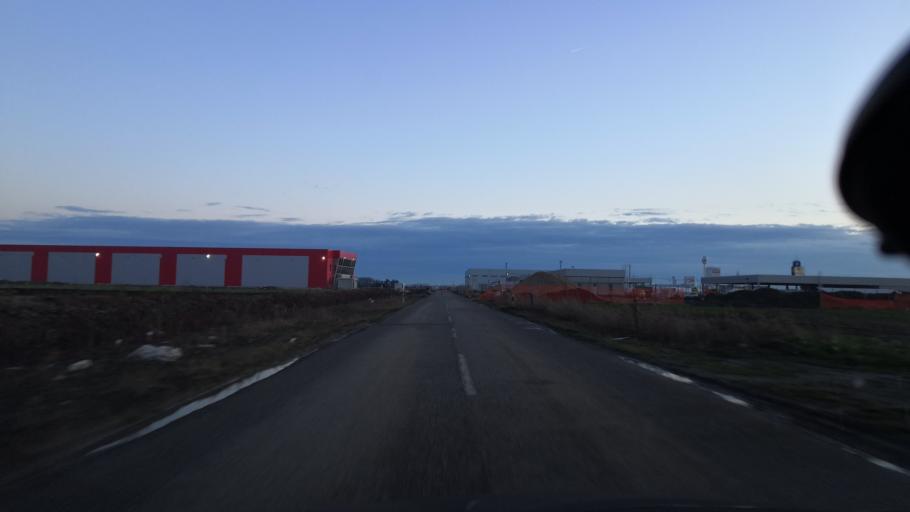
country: RS
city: Simanovci
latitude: 44.8880
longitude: 20.1110
